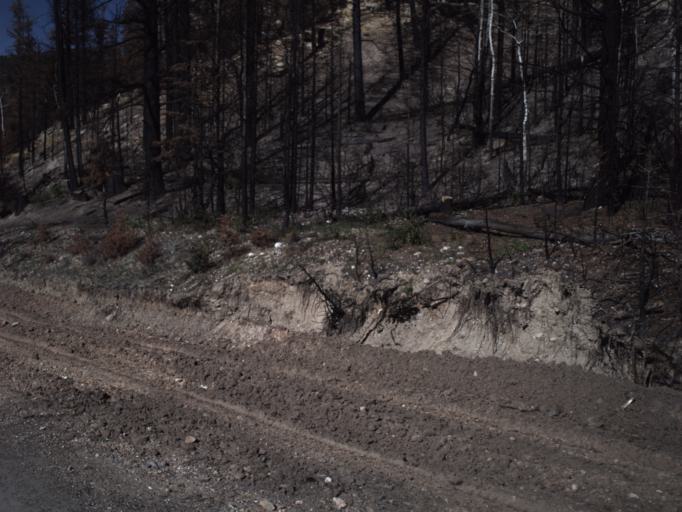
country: US
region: Utah
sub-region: Iron County
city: Parowan
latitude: 37.7445
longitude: -112.8382
